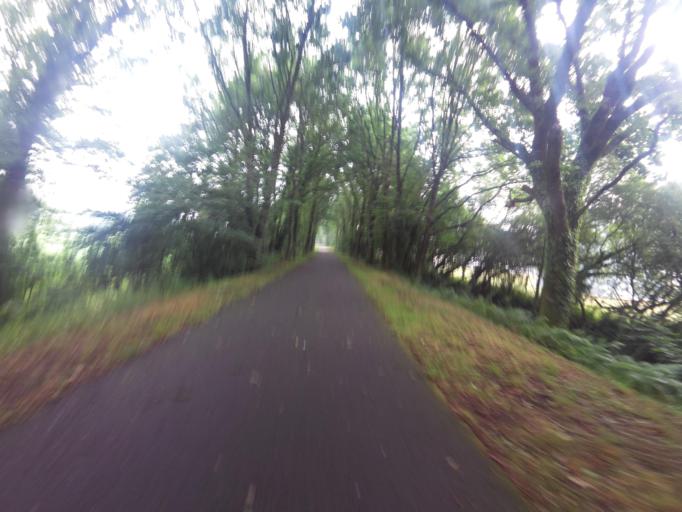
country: FR
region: Brittany
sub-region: Departement du Morbihan
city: Guillac
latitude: 47.8889
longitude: -2.4360
